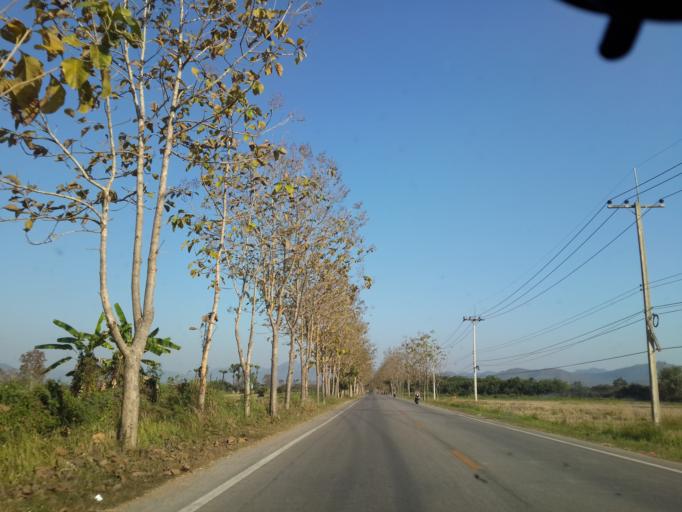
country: TH
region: Chiang Mai
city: San Kamphaeng
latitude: 18.7278
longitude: 99.1396
